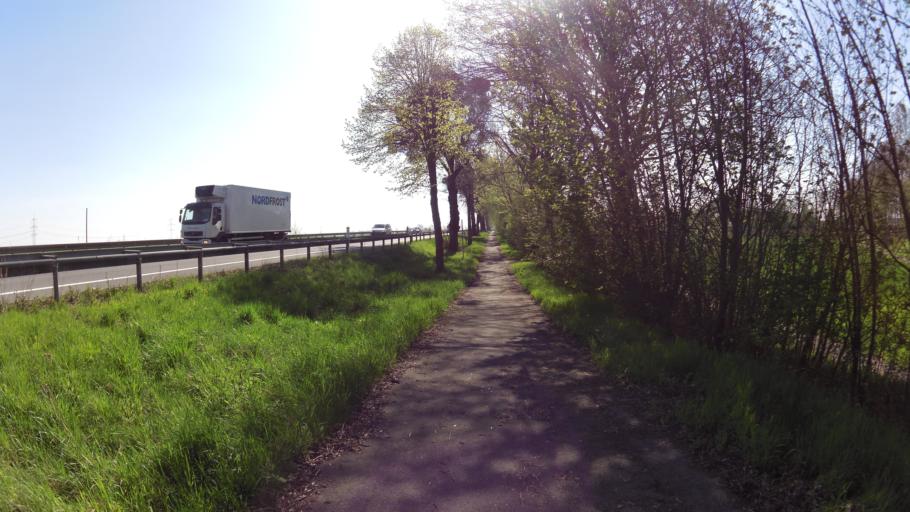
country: DE
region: North Rhine-Westphalia
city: Baesweiler
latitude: 50.9453
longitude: 6.1880
